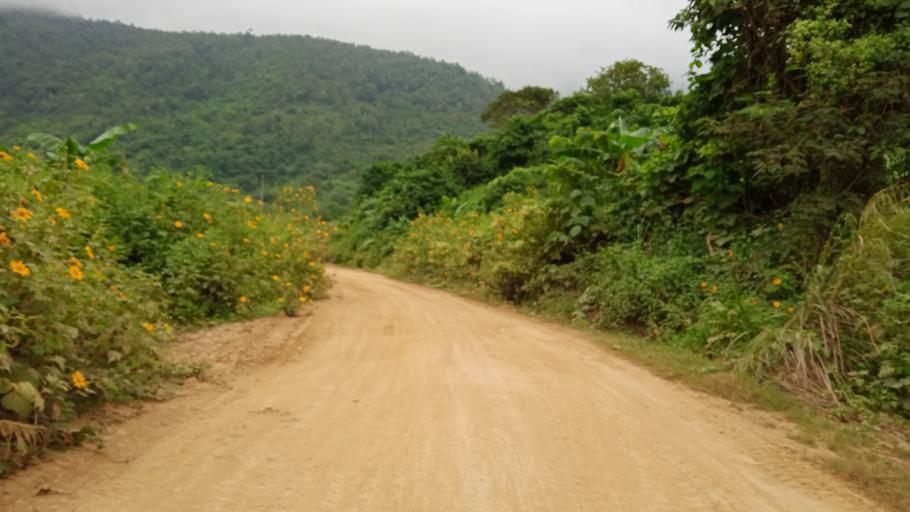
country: LA
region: Xiangkhoang
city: Phonsavan
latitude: 19.0936
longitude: 102.9877
